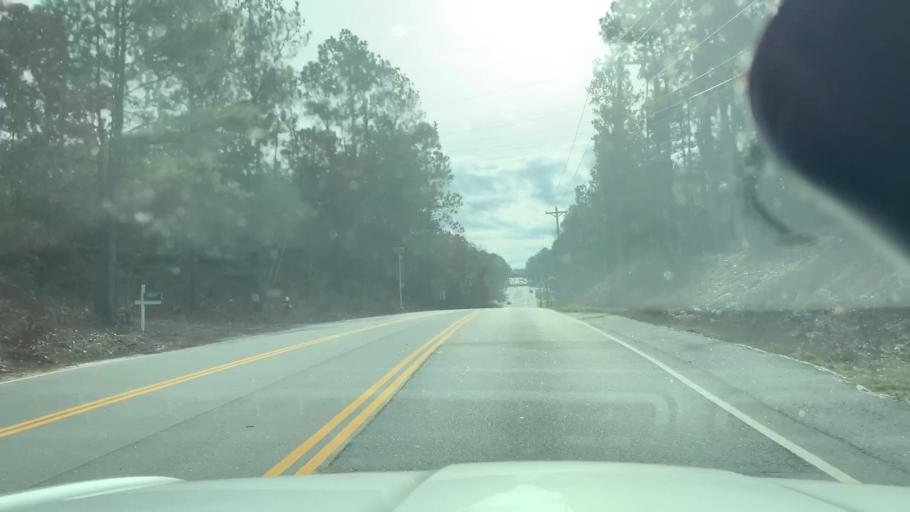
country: US
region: South Carolina
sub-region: Richland County
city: Woodfield
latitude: 34.0748
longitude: -80.9178
